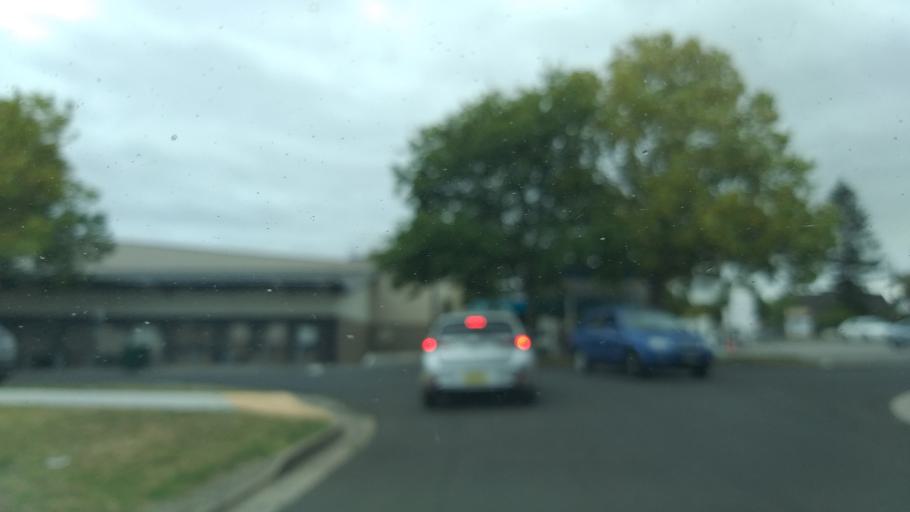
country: AU
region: New South Wales
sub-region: Wollongong
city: Berkeley
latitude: -34.4802
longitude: 150.8468
